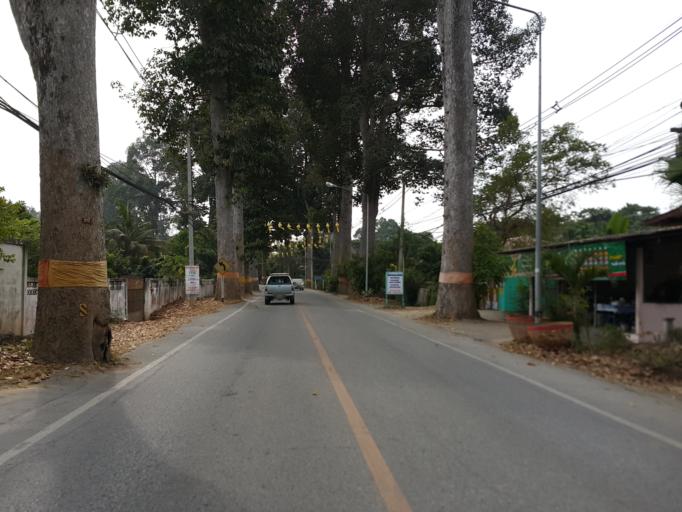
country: TH
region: Chiang Mai
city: Saraphi
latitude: 18.6801
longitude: 99.0423
